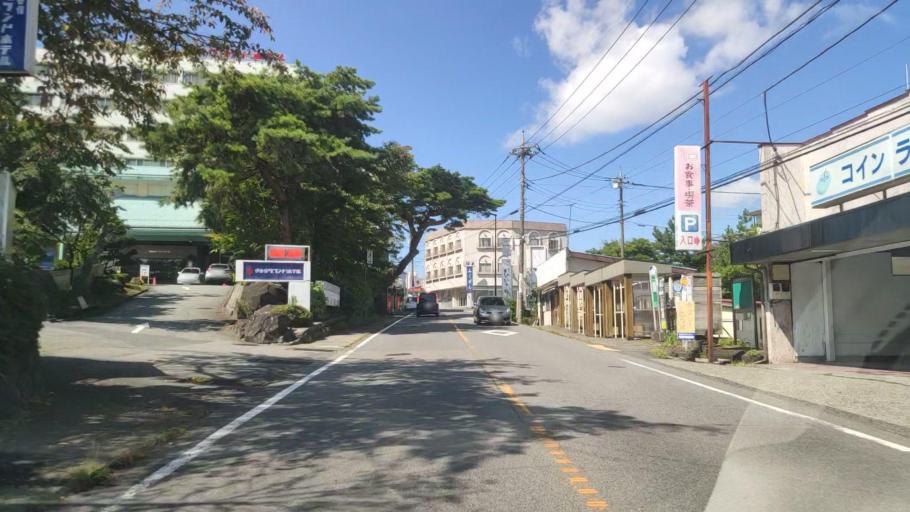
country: JP
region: Gunma
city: Shibukawa
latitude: 36.4998
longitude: 138.9259
